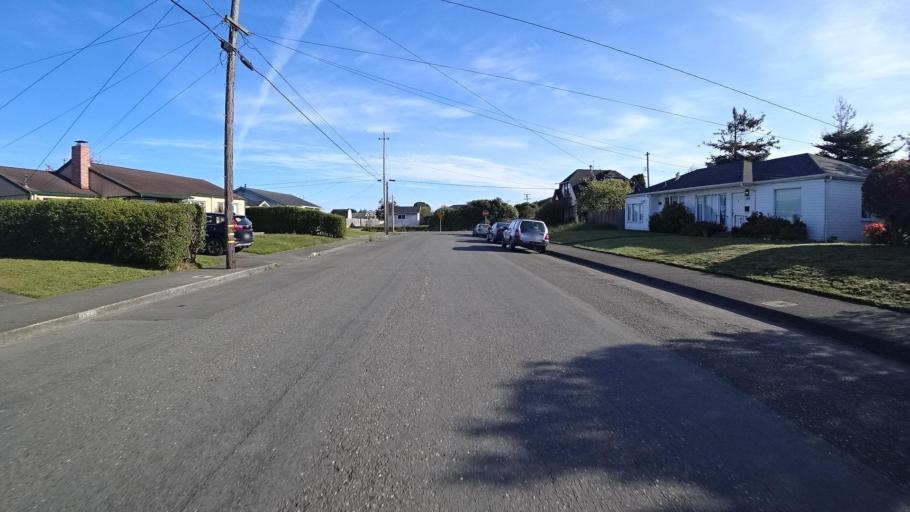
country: US
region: California
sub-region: Humboldt County
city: Bayview
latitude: 40.7753
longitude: -124.1762
